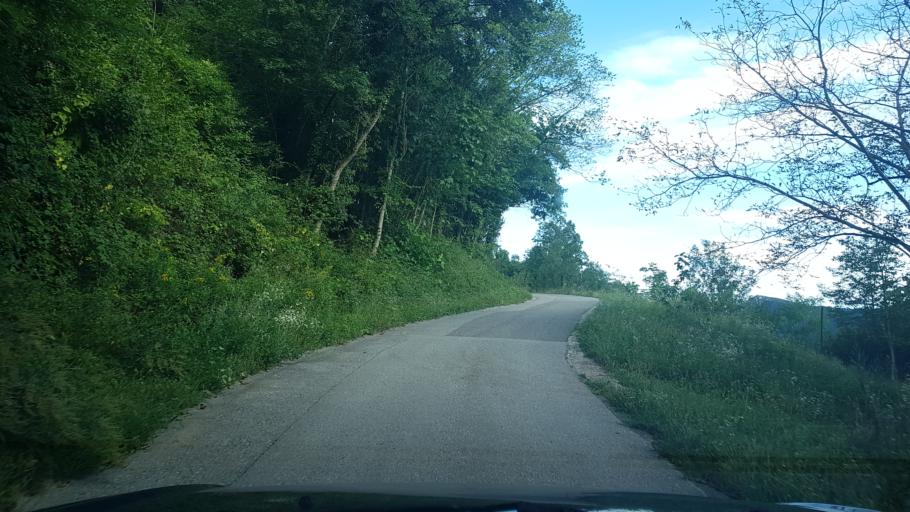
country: SI
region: Kanal
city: Deskle
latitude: 46.0300
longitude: 13.6005
